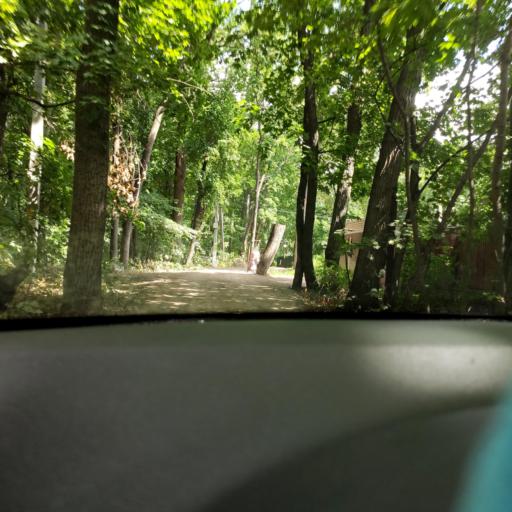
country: RU
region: Samara
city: Samara
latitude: 53.2946
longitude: 50.2285
